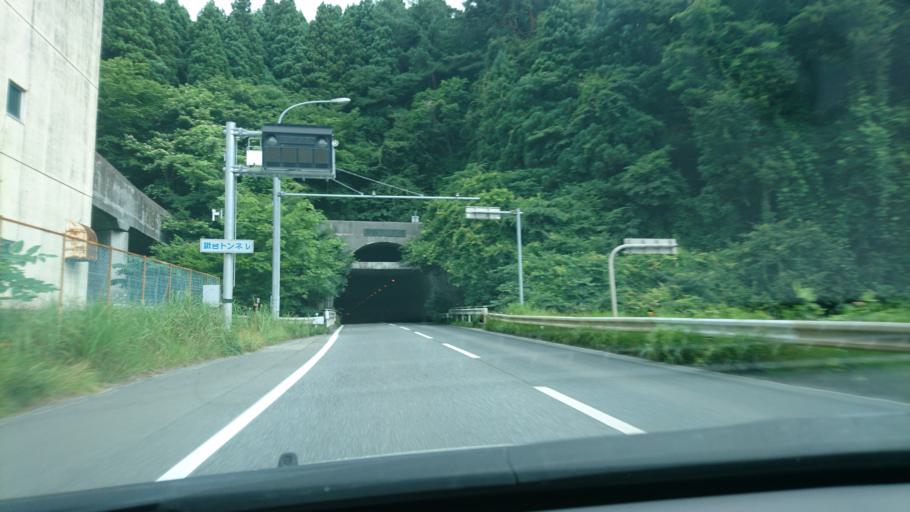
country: JP
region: Iwate
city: Kamaishi
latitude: 39.1633
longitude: 141.8535
